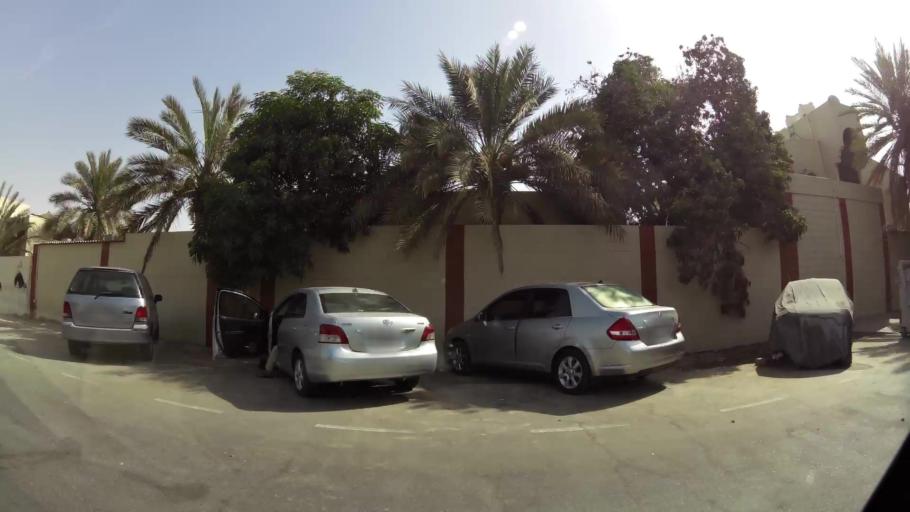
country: AE
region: Dubai
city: Dubai
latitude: 25.1670
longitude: 55.2443
